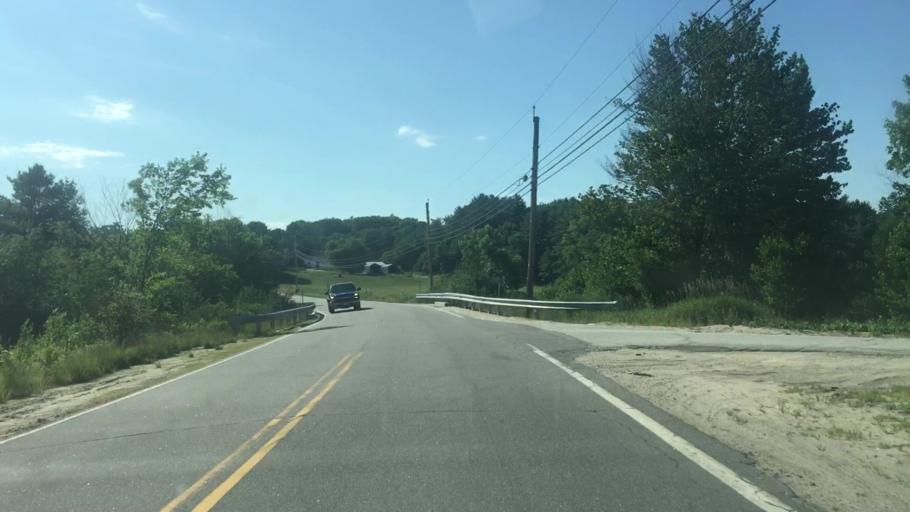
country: US
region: Maine
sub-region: York County
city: Buxton
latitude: 43.6294
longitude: -70.5547
